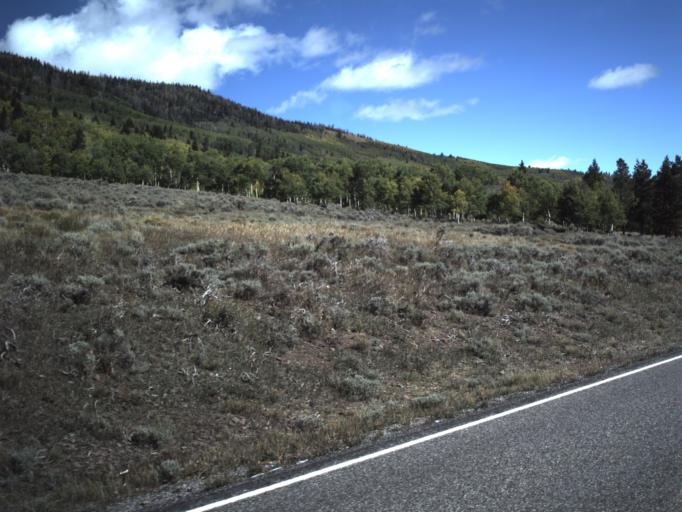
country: US
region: Utah
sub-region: Wayne County
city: Loa
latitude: 38.5506
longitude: -111.7216
